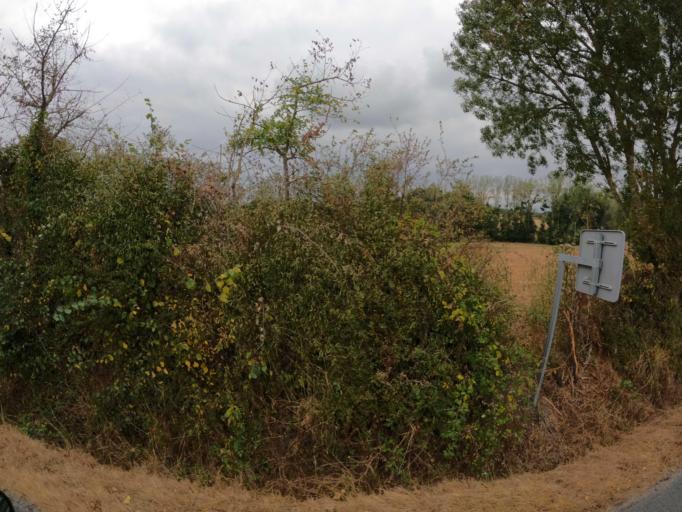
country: FR
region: Pays de la Loire
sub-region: Departement de la Vendee
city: Les Landes-Genusson
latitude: 46.9777
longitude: -1.1125
